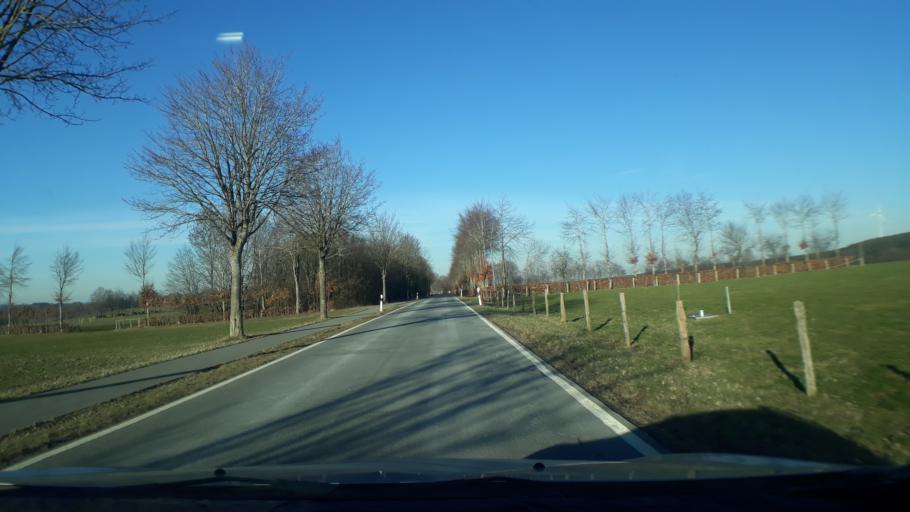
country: DE
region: North Rhine-Westphalia
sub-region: Regierungsbezirk Koln
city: Monschau
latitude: 50.5372
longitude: 6.2809
